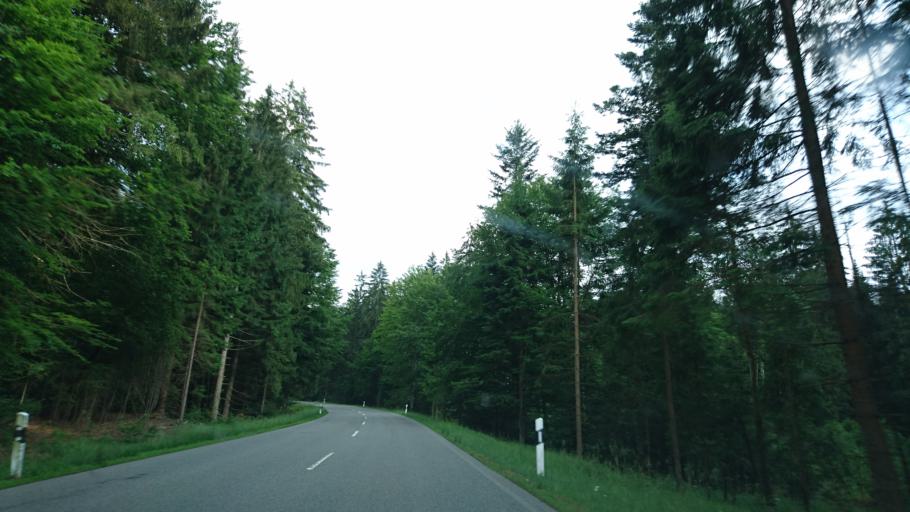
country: DE
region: Bavaria
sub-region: Lower Bavaria
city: Neuschonau
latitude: 48.9149
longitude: 13.4582
